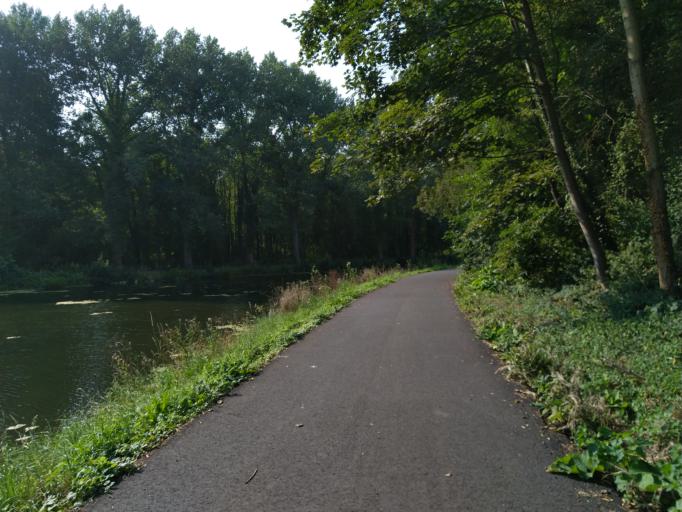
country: BE
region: Wallonia
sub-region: Province du Hainaut
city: Seneffe
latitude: 50.5742
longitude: 4.2543
